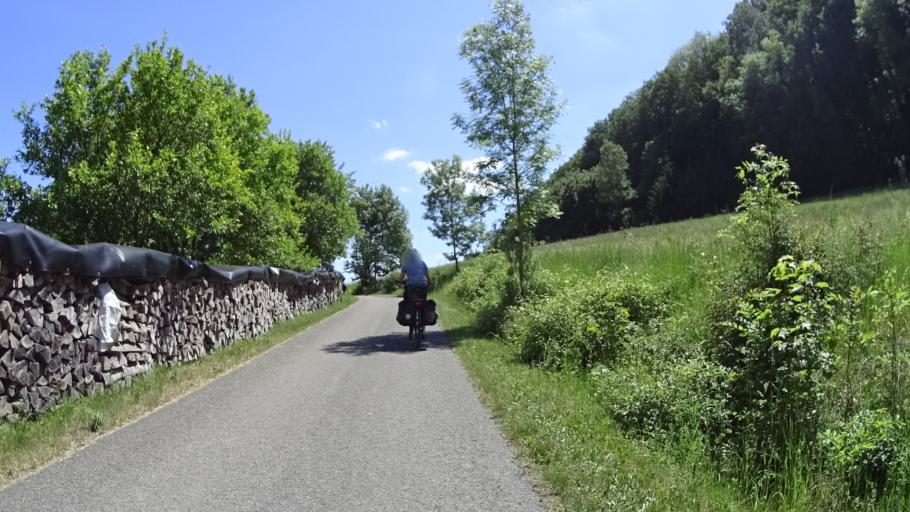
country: DE
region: Bavaria
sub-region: Regierungsbezirk Mittelfranken
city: Adelshofen
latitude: 49.4459
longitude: 10.1157
